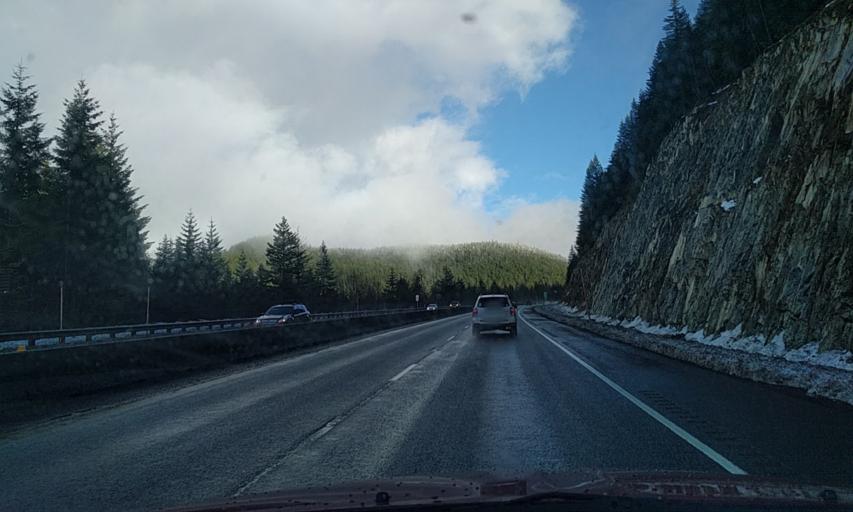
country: US
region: Oregon
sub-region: Clackamas County
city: Mount Hood Village
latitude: 45.3114
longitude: -121.8004
